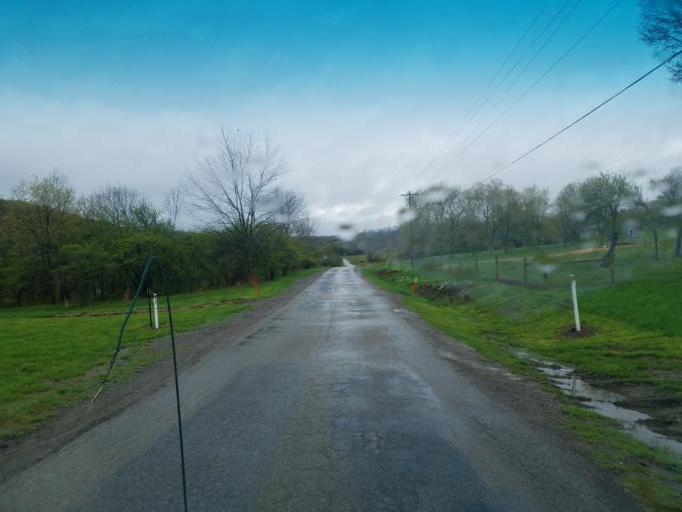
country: US
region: Pennsylvania
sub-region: Tioga County
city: Westfield
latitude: 41.9750
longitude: -77.6710
